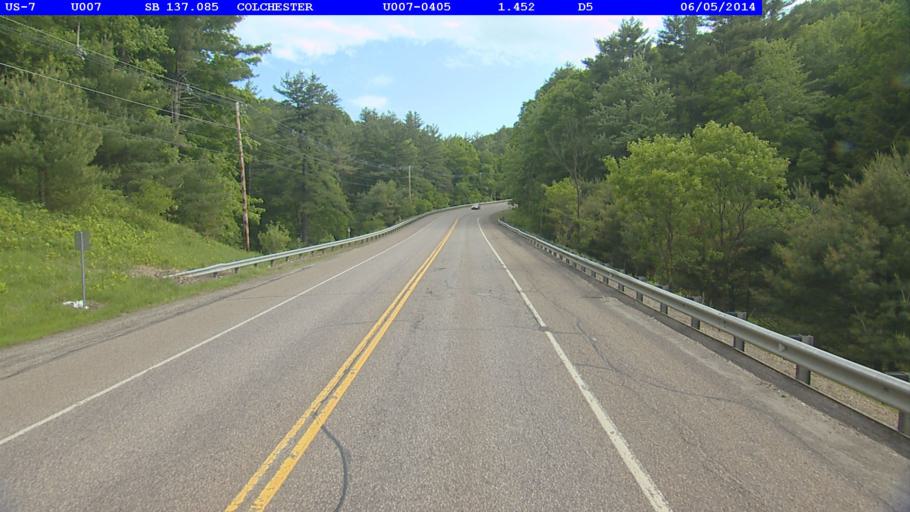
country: US
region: Vermont
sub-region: Chittenden County
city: Winooski
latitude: 44.5211
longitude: -73.1730
